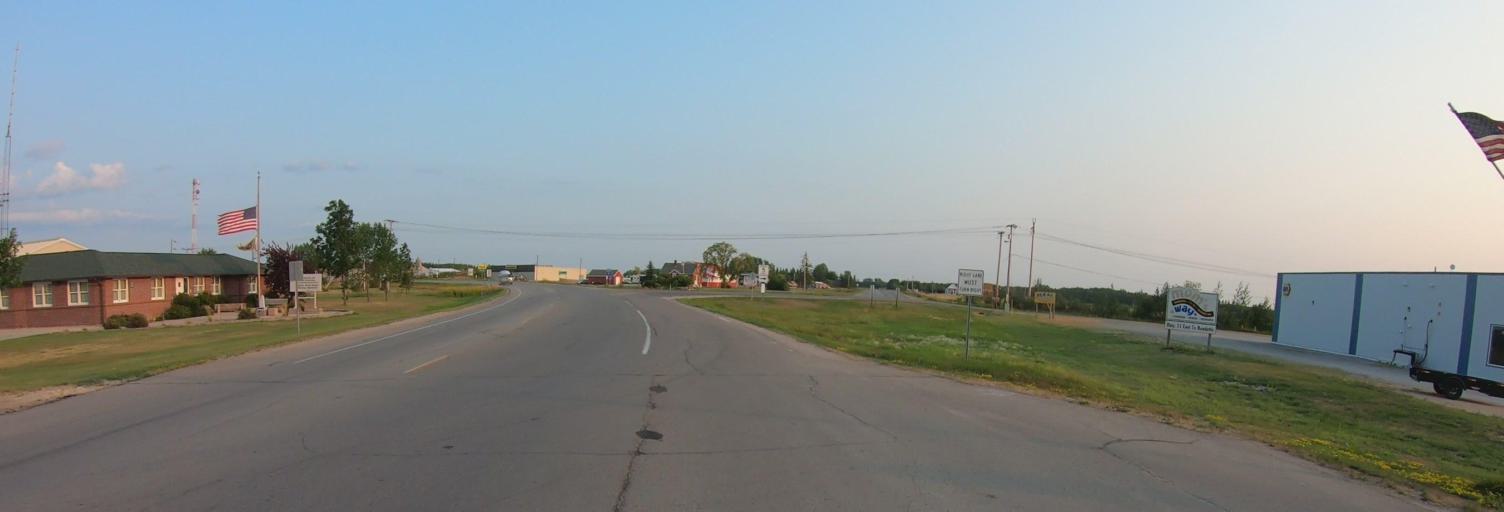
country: US
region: Minnesota
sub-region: Roseau County
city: Warroad
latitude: 48.8989
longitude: -95.3200
